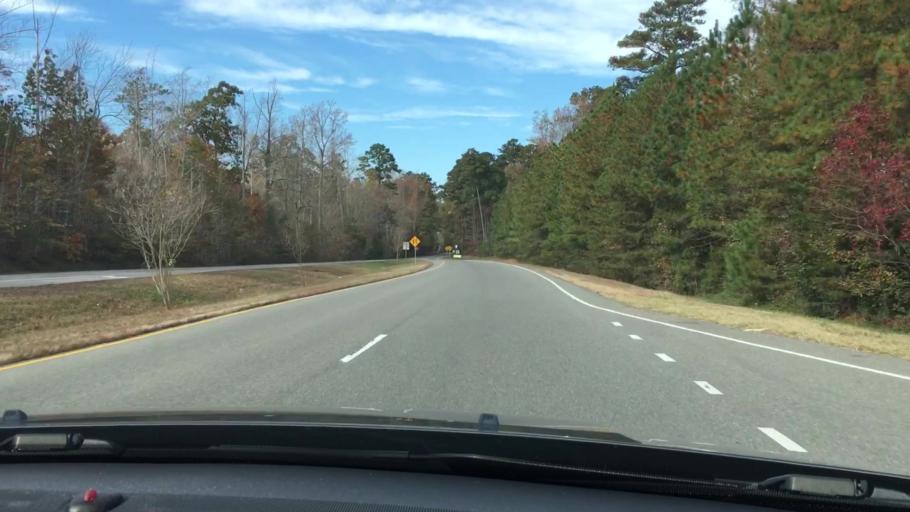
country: US
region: Virginia
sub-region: King William County
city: West Point
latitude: 37.4286
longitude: -76.8294
